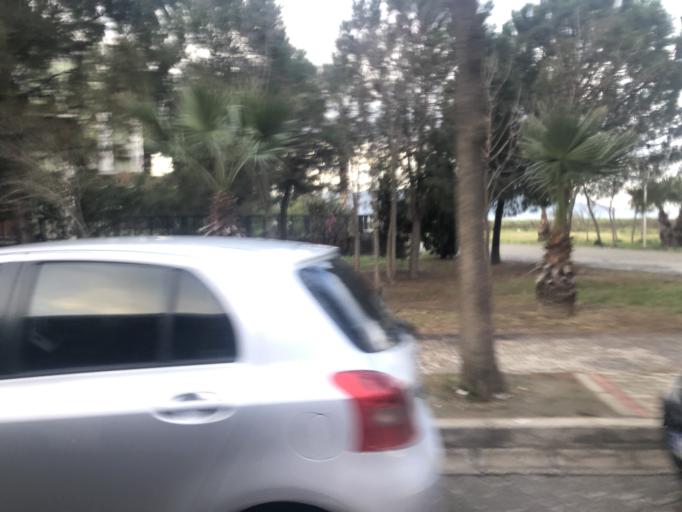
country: TR
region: Izmir
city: Karsiyaka
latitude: 38.4678
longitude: 27.0669
